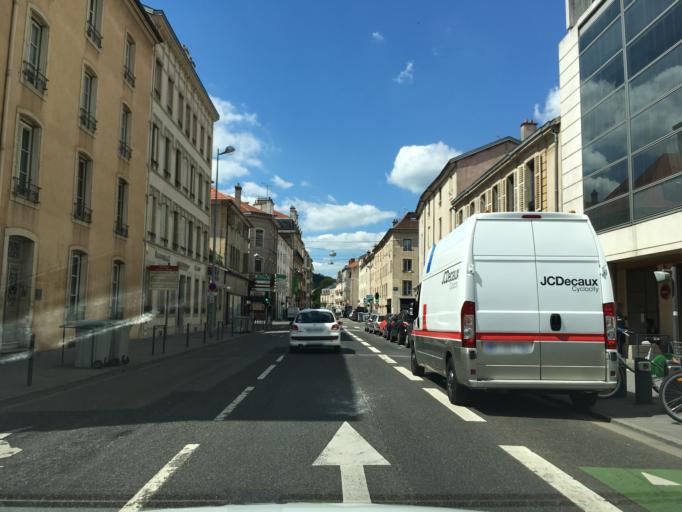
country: FR
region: Lorraine
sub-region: Departement de Meurthe-et-Moselle
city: Nancy
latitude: 48.6895
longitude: 6.1723
